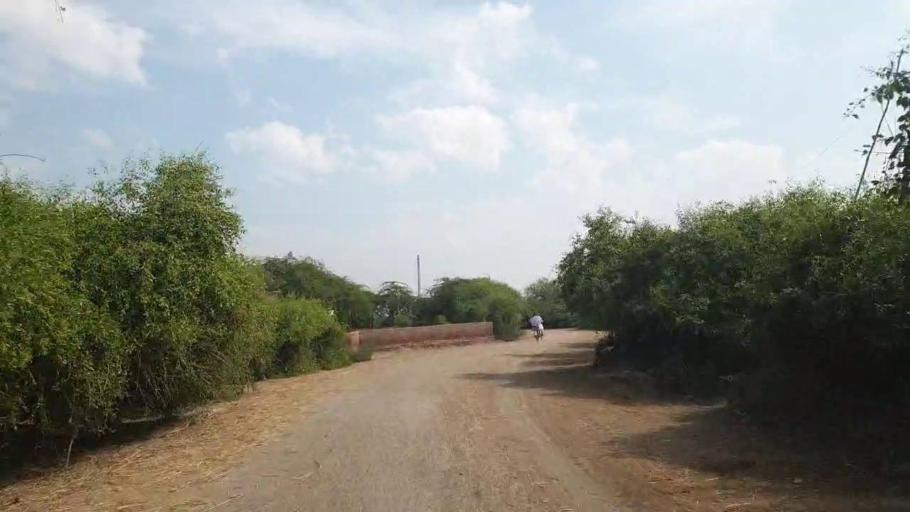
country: PK
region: Sindh
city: Rajo Khanani
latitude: 24.9372
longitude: 68.9913
